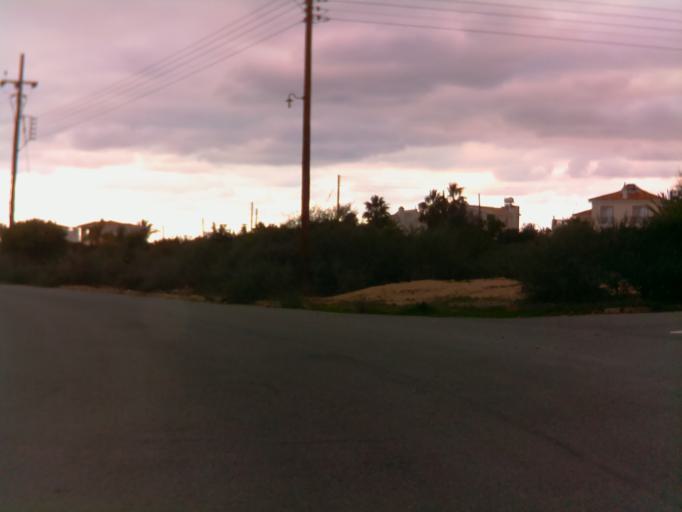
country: CY
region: Pafos
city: Pegeia
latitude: 34.8857
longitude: 32.3359
